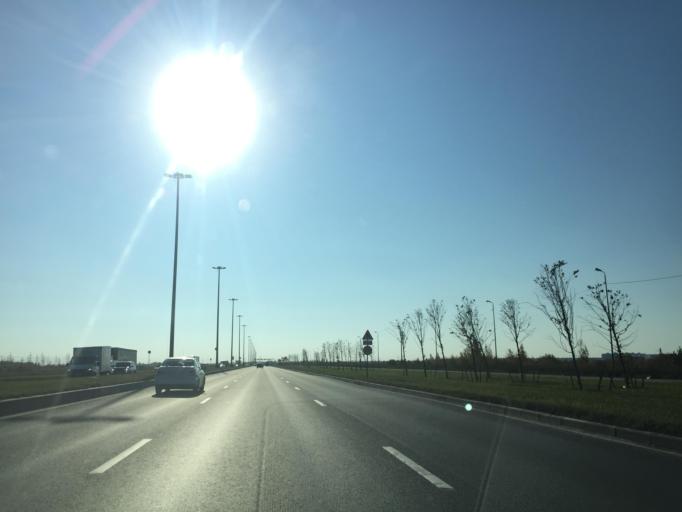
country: RU
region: St.-Petersburg
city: Petro-Slavyanka
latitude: 59.7782
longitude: 30.4980
